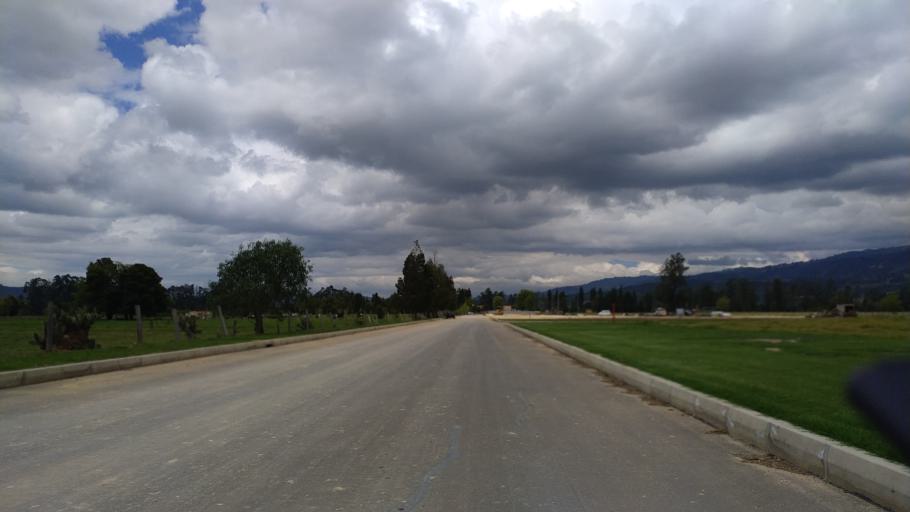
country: CO
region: Boyaca
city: Duitama
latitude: 5.7969
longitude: -73.0663
